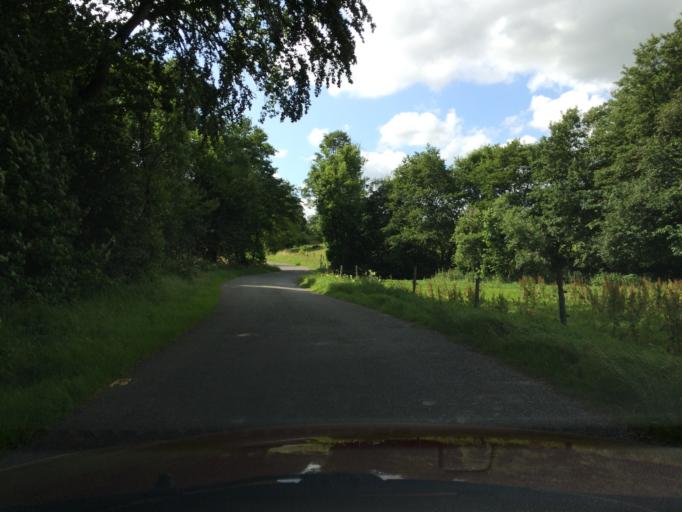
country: DK
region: Central Jutland
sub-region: Skanderborg Kommune
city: Galten
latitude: 56.1612
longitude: 9.8599
